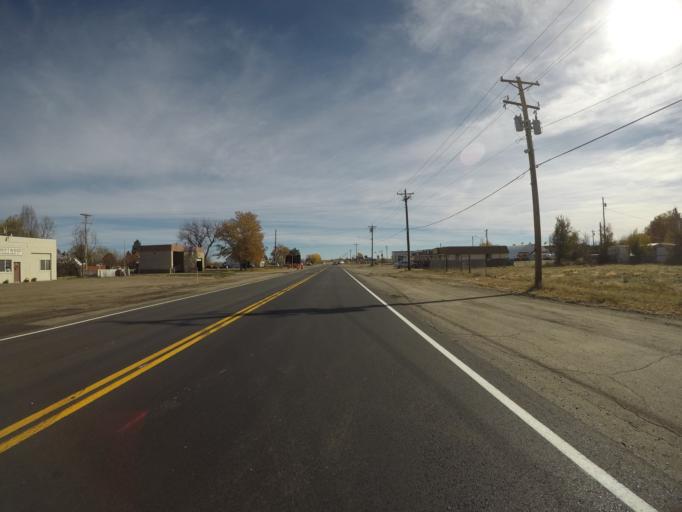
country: US
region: Colorado
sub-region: Adams County
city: Strasburg
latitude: 39.7384
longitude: -104.3225
